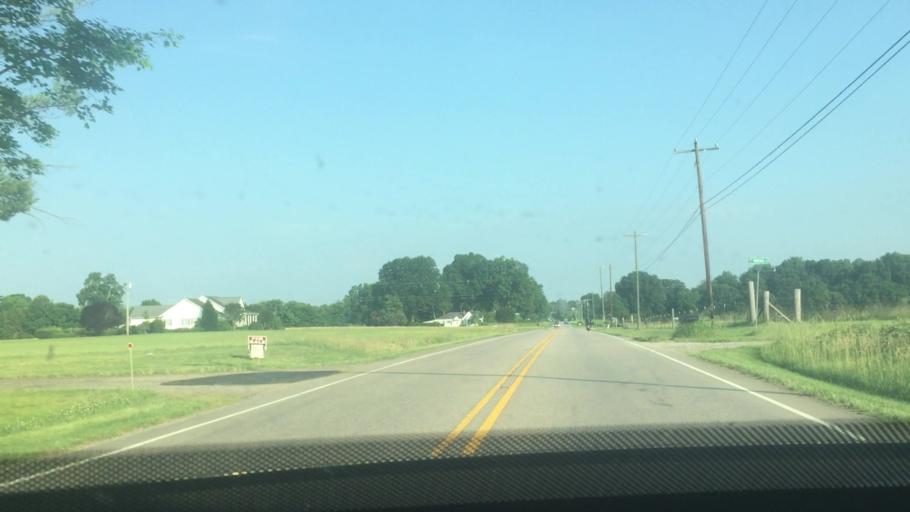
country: US
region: North Carolina
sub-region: Iredell County
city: Mooresville
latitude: 35.5866
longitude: -80.7454
